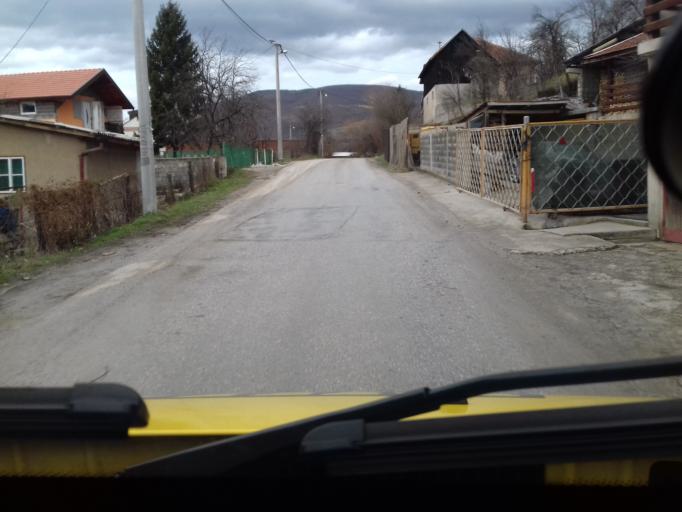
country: BA
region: Federation of Bosnia and Herzegovina
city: Zenica
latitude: 44.1732
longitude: 17.9767
